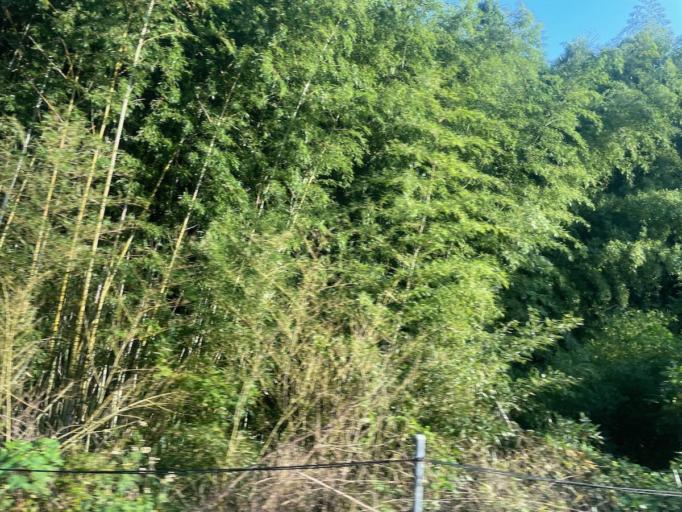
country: JP
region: Mie
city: Hisai-motomachi
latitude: 34.6622
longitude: 136.4222
